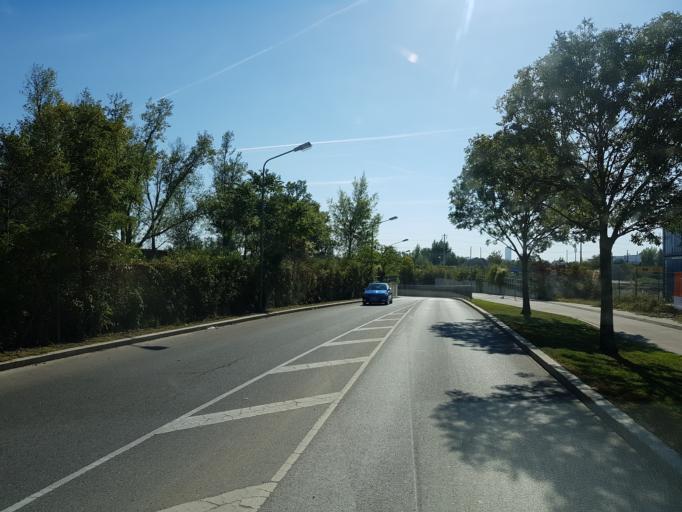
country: AT
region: Lower Austria
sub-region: Politischer Bezirk Wien-Umgebung
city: Gerasdorf bei Wien
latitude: 48.2754
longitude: 16.4321
